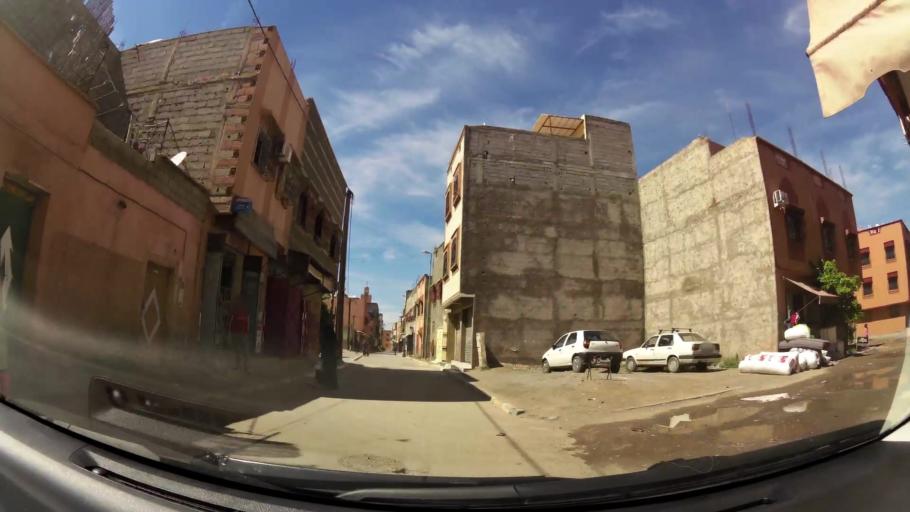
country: MA
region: Marrakech-Tensift-Al Haouz
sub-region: Marrakech
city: Marrakesh
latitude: 31.5971
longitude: -7.9601
